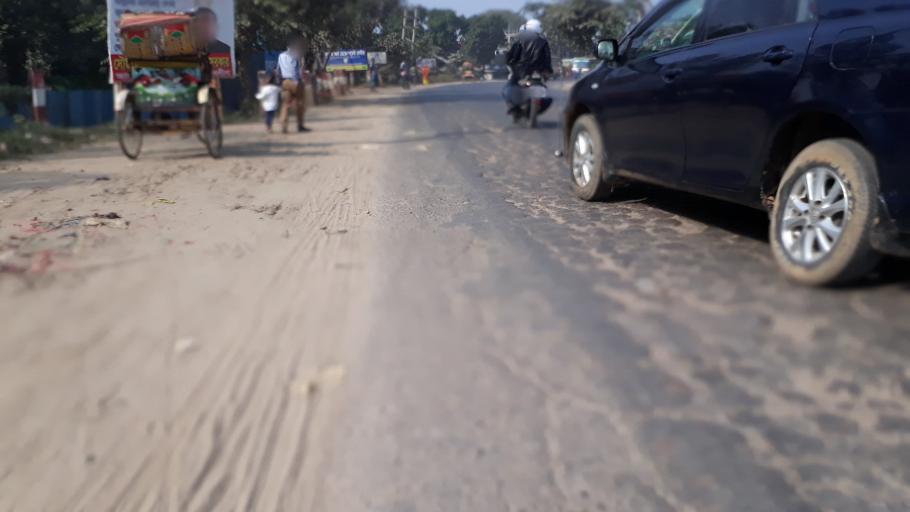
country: BD
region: Dhaka
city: Tungi
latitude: 23.9067
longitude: 90.3216
